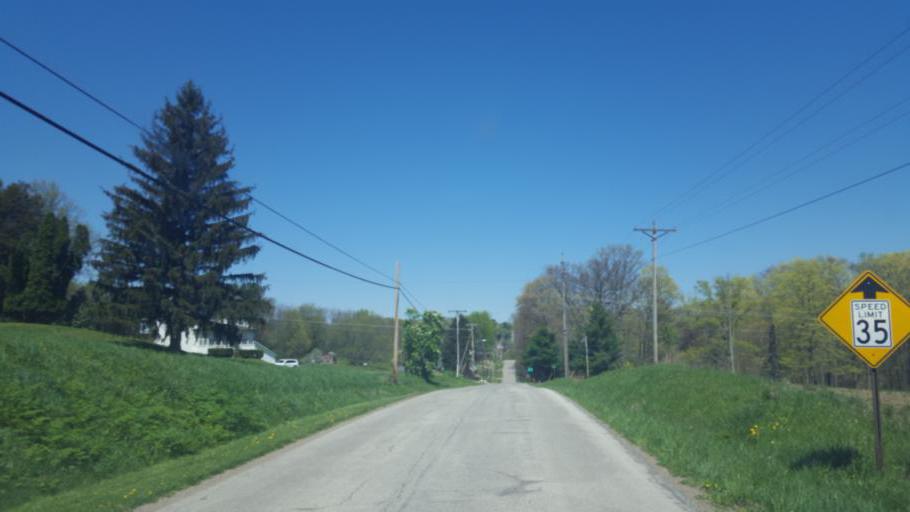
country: US
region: Ohio
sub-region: Richland County
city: Lincoln Heights
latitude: 40.6961
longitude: -82.4170
